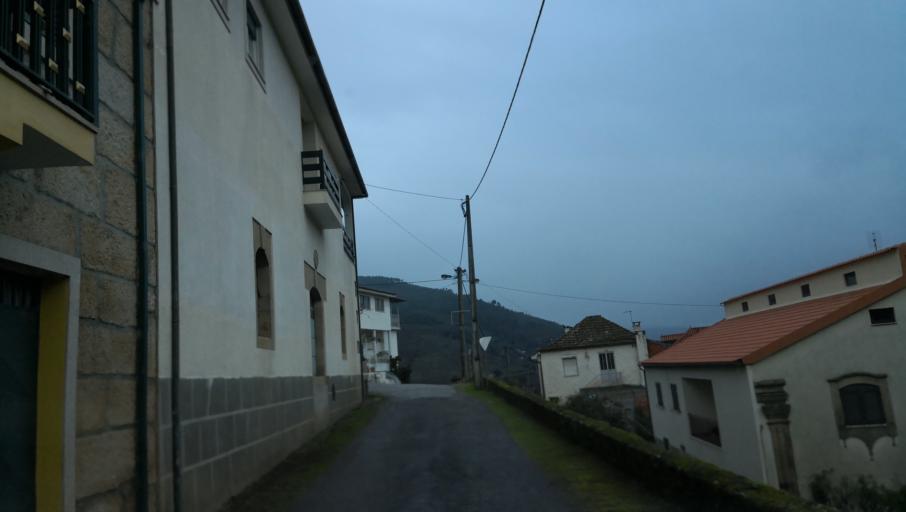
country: PT
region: Vila Real
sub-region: Vila Real
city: Vila Real
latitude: 41.2365
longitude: -7.7396
